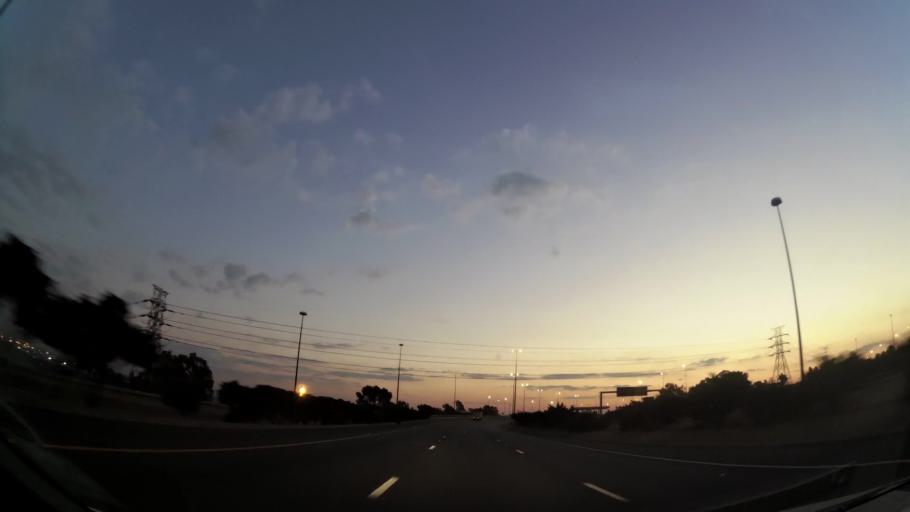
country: ZA
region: Gauteng
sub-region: Ekurhuleni Metropolitan Municipality
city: Germiston
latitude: -26.2513
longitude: 28.1448
